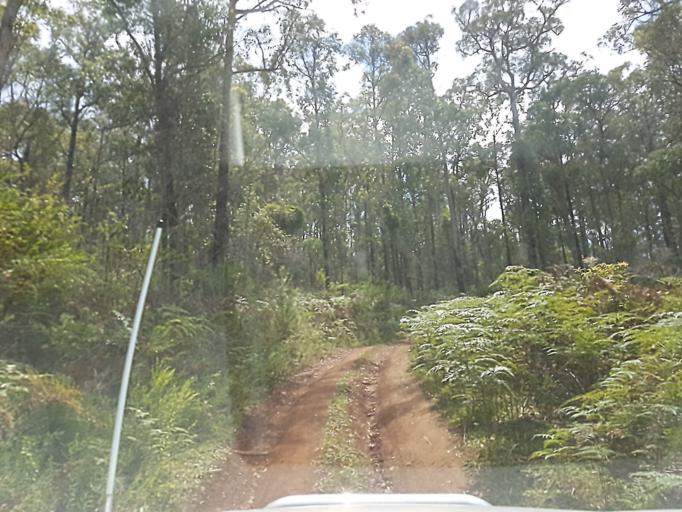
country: AU
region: Victoria
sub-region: East Gippsland
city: Lakes Entrance
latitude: -37.3472
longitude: 148.3571
